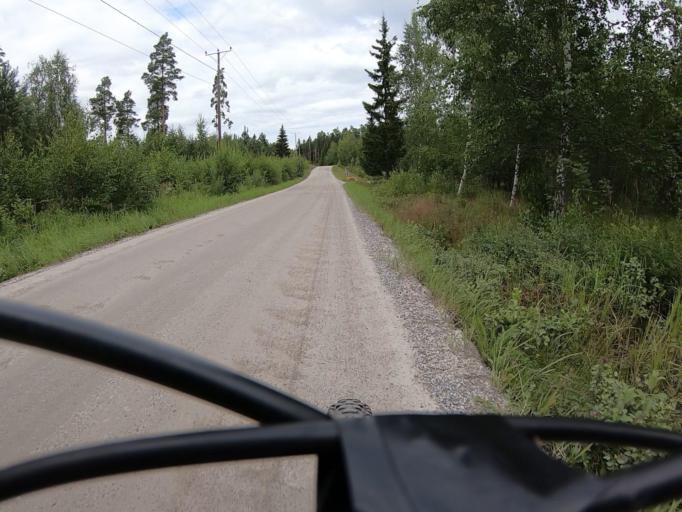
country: FI
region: Varsinais-Suomi
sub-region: Vakka-Suomi
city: Uusikaupunki
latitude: 60.8409
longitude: 21.3852
